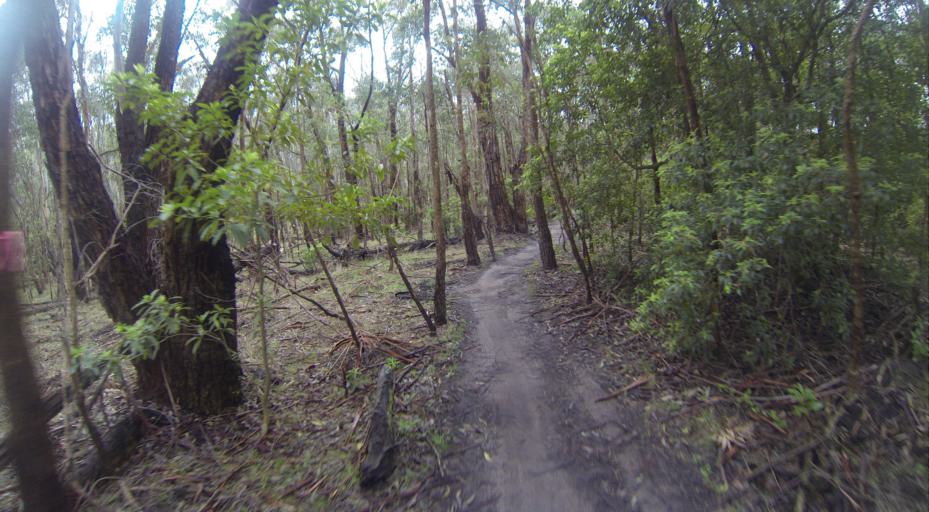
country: AU
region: Victoria
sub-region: Yarra Ranges
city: Lysterfield
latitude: -37.9389
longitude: 145.3036
